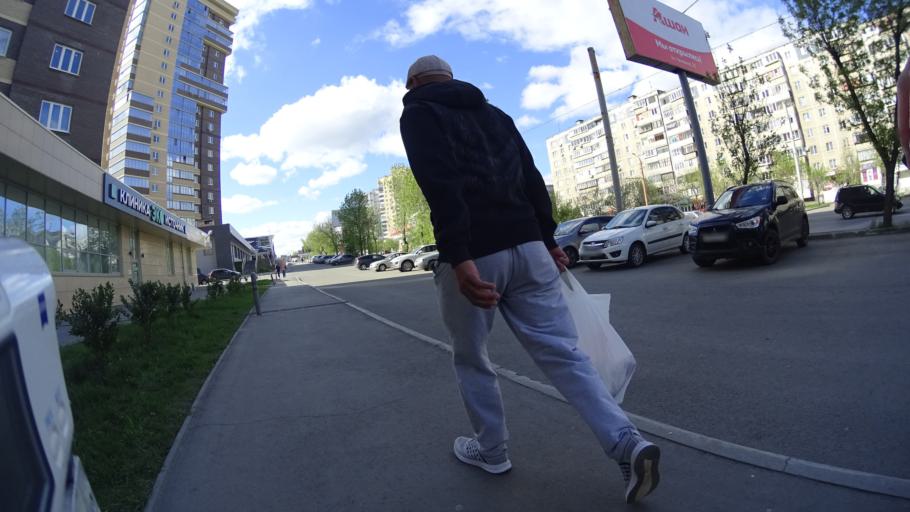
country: RU
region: Chelyabinsk
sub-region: Gorod Chelyabinsk
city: Chelyabinsk
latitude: 55.1785
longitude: 61.2974
